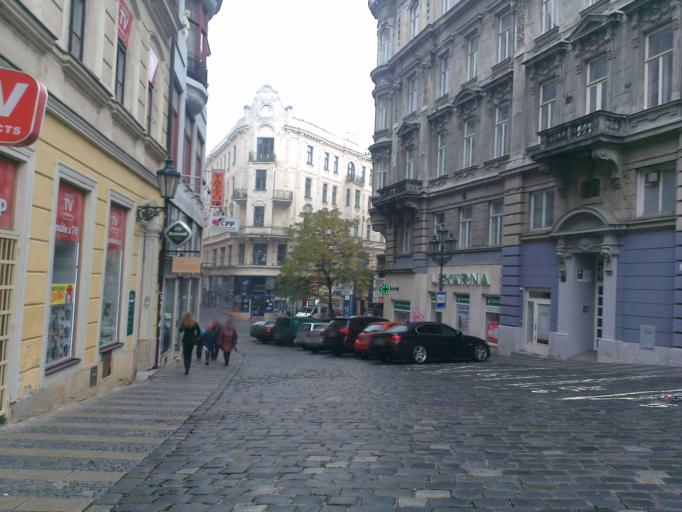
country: CZ
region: South Moravian
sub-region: Mesto Brno
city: Brno
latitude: 49.1917
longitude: 16.6099
